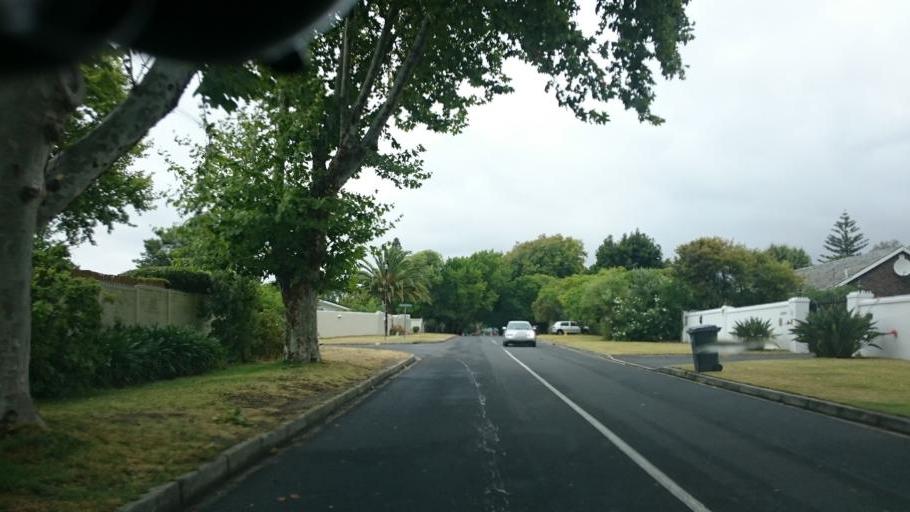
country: ZA
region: Western Cape
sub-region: City of Cape Town
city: Bergvliet
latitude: -34.0268
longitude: 18.4512
